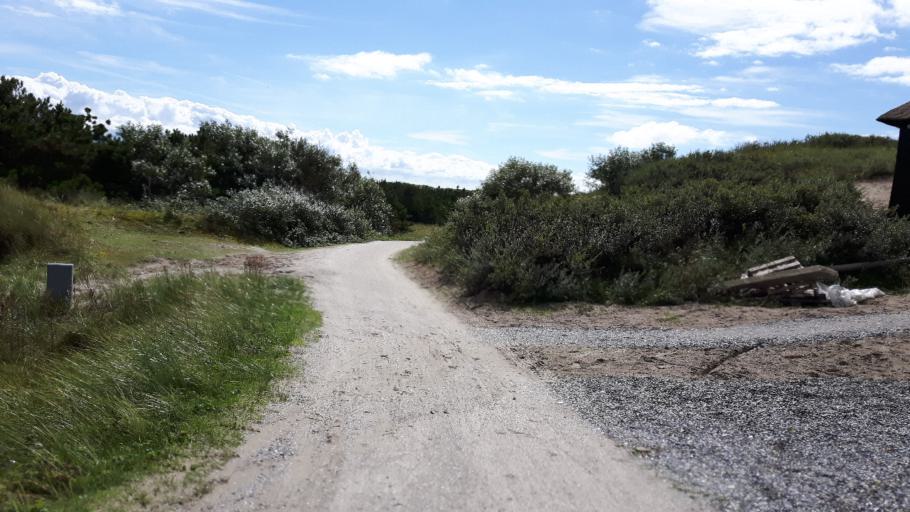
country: NL
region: Friesland
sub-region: Gemeente Ameland
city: Hollum
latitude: 53.4479
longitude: 5.6175
